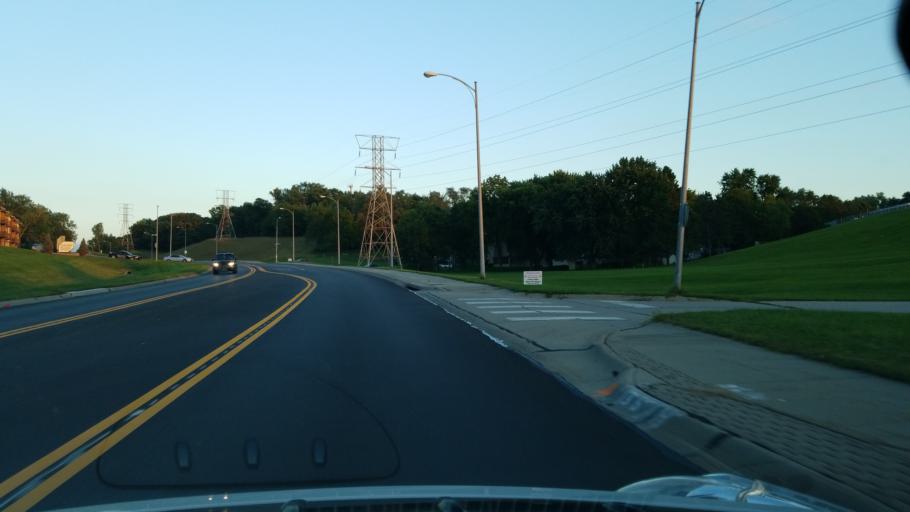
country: US
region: Nebraska
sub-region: Sarpy County
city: Bellevue
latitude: 41.1484
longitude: -95.9030
